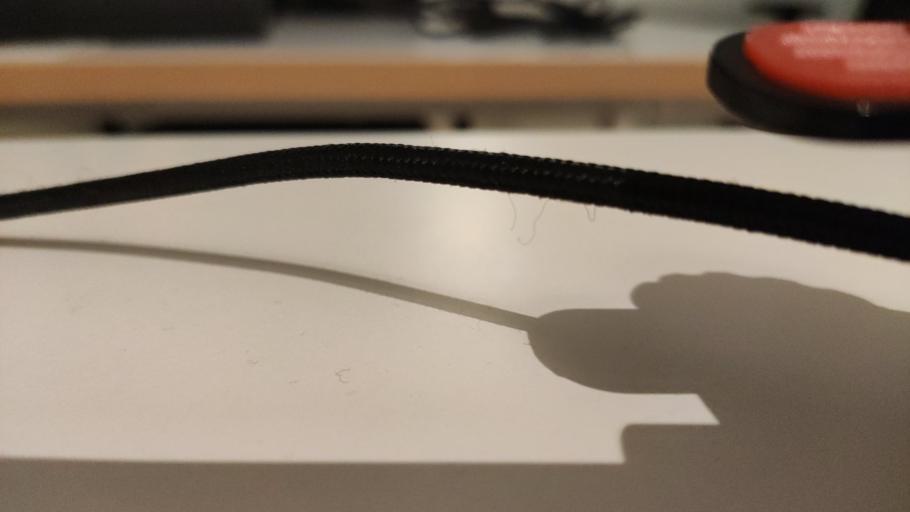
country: RU
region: Moskovskaya
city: Novosin'kovo
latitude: 56.3944
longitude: 37.2805
